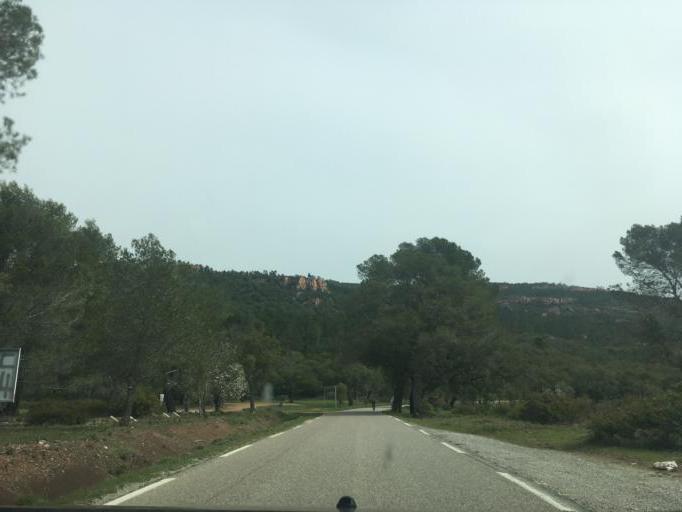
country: FR
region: Provence-Alpes-Cote d'Azur
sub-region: Departement du Var
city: Bagnols-en-Foret
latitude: 43.5151
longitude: 6.6296
